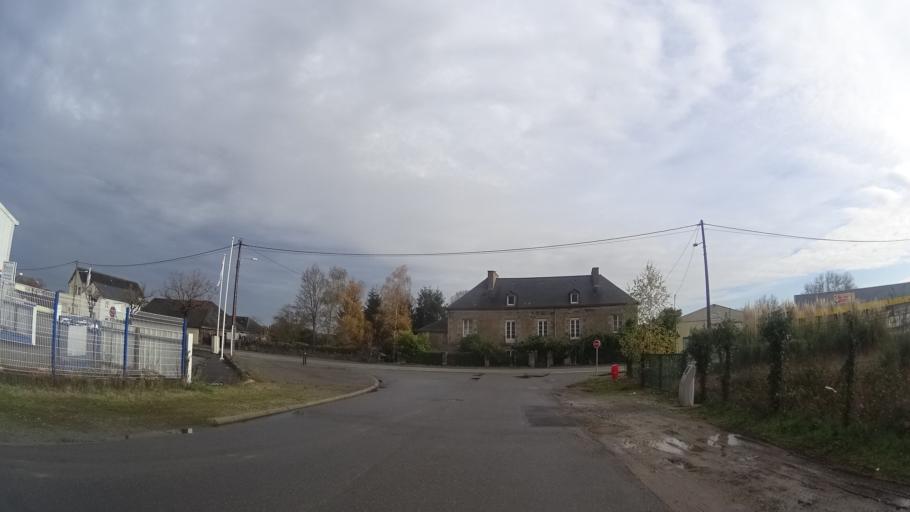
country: FR
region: Brittany
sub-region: Departement d'Ille-et-Vilaine
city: Redon
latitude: 47.6407
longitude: -2.0929
